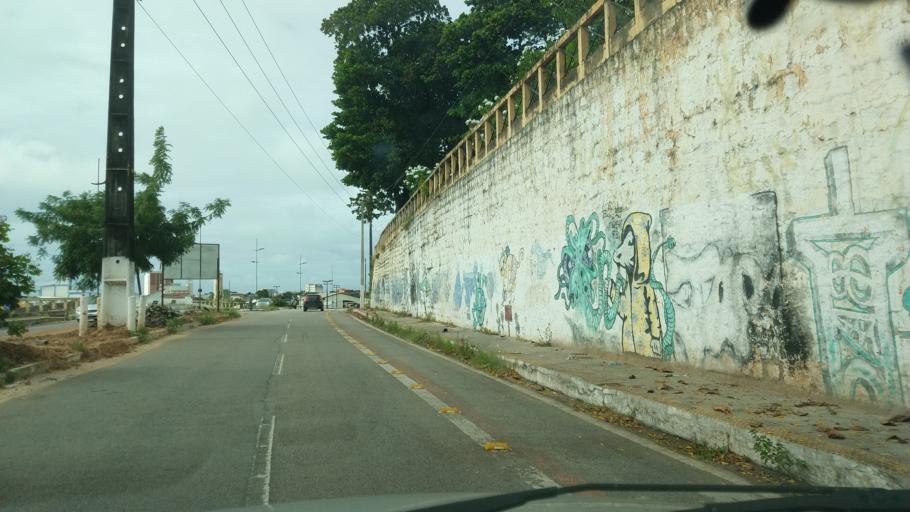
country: BR
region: Rio Grande do Norte
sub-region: Natal
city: Natal
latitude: -5.7831
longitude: -35.2098
